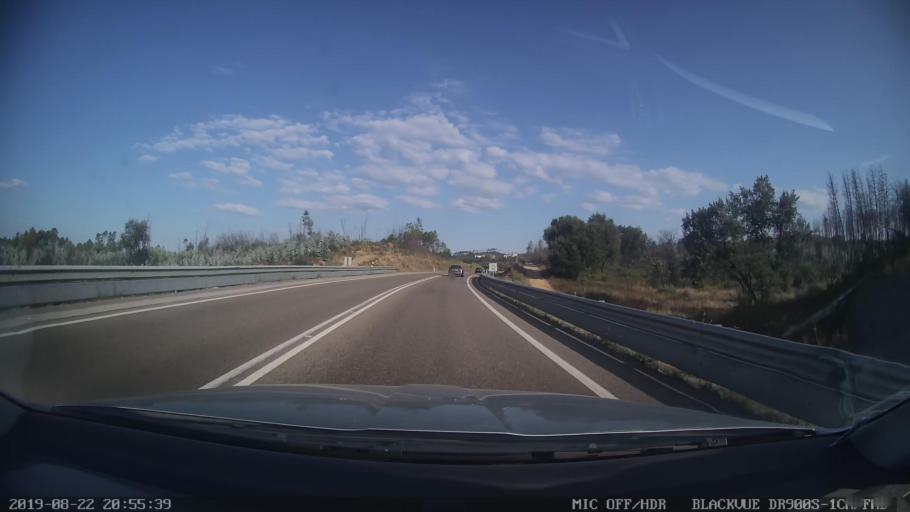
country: PT
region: Castelo Branco
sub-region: Serta
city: Serta
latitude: 39.7818
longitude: -8.0375
